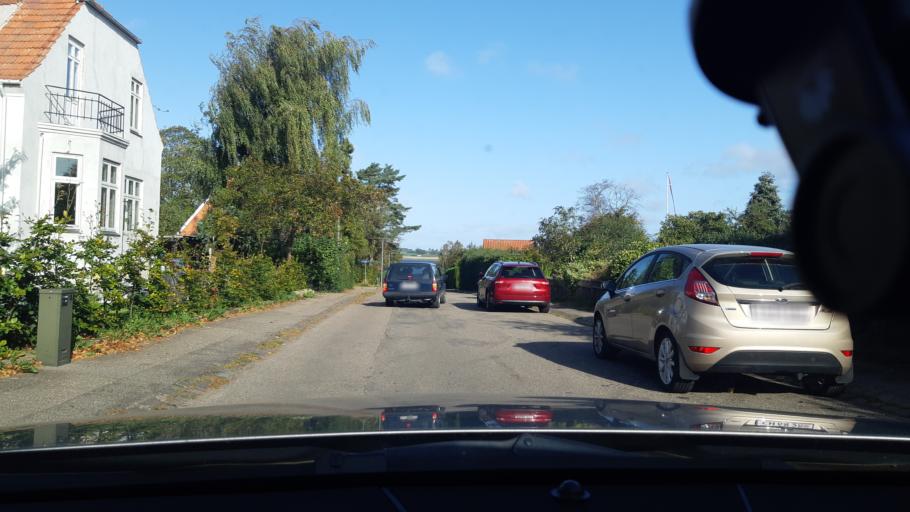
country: DK
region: Zealand
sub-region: Holbaek Kommune
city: Holbaek
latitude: 55.7168
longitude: 11.6875
